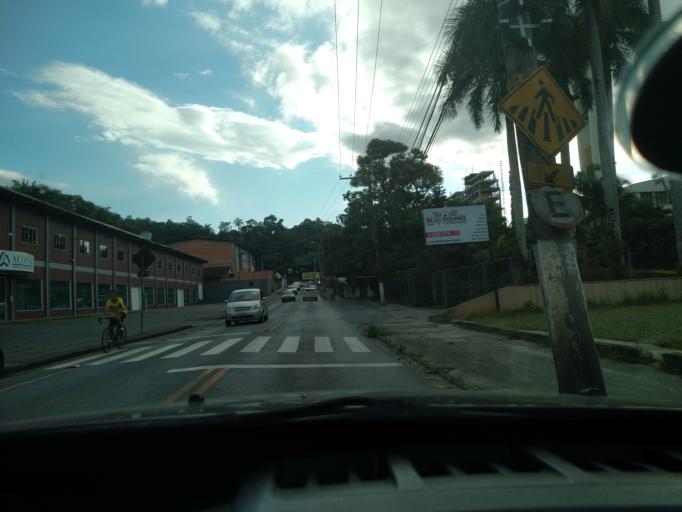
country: BR
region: Santa Catarina
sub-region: Blumenau
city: Blumenau
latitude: -26.8886
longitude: -49.0858
